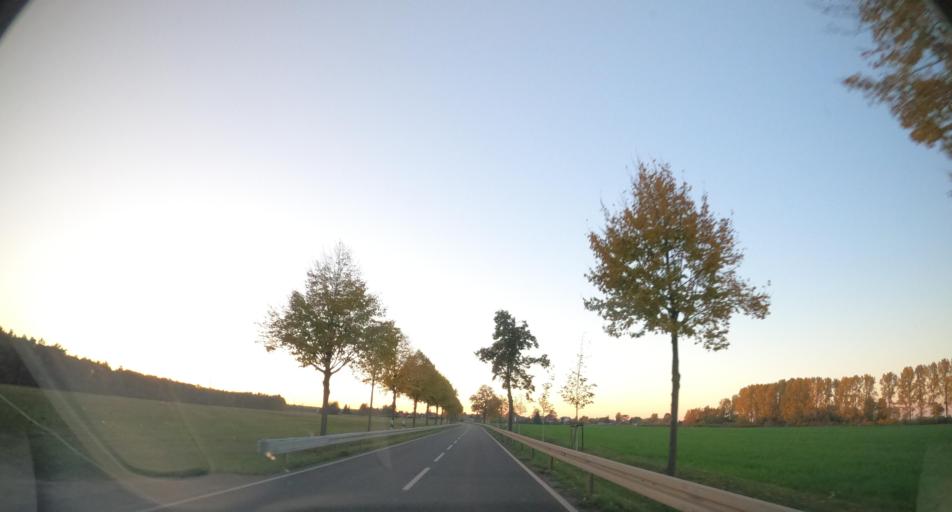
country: DE
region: Mecklenburg-Vorpommern
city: Ueckermunde
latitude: 53.7654
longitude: 13.9841
